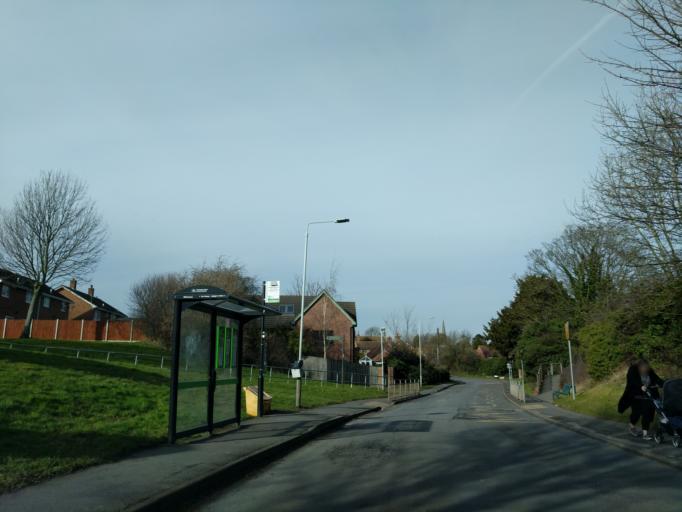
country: GB
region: England
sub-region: Nottinghamshire
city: Cotgrave
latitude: 52.9086
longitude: -1.0417
